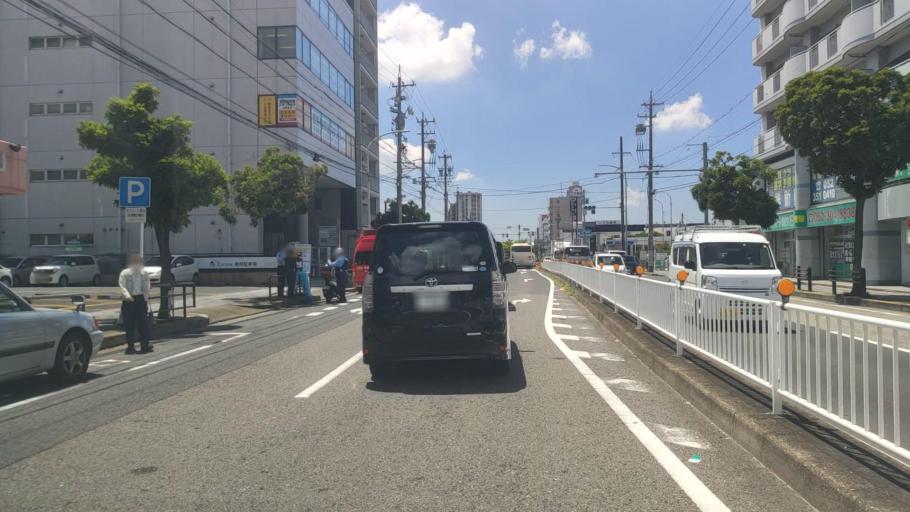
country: JP
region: Aichi
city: Kanie
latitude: 35.1412
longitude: 136.8533
